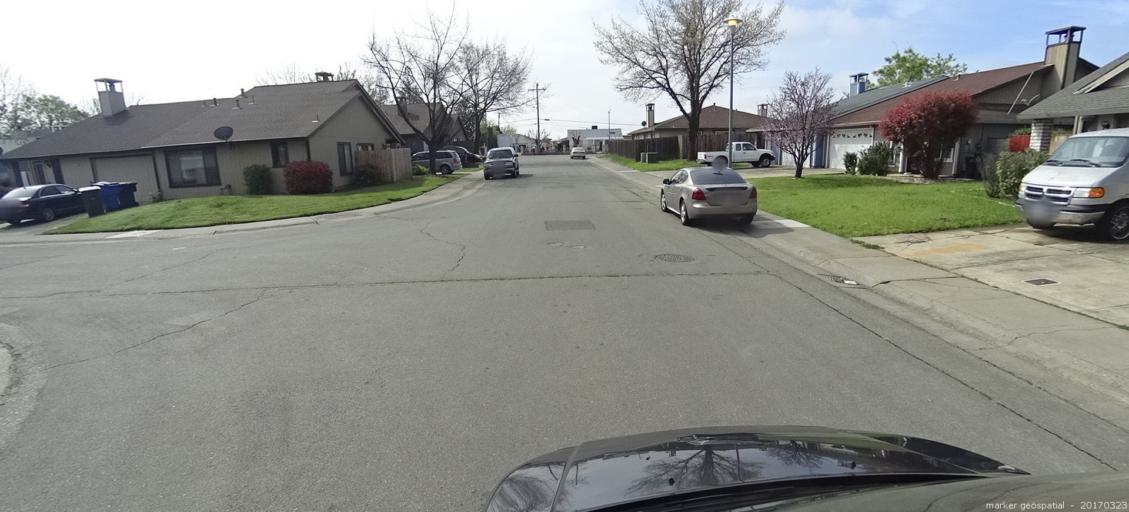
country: US
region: California
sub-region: Sacramento County
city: Florin
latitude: 38.5068
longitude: -121.4318
